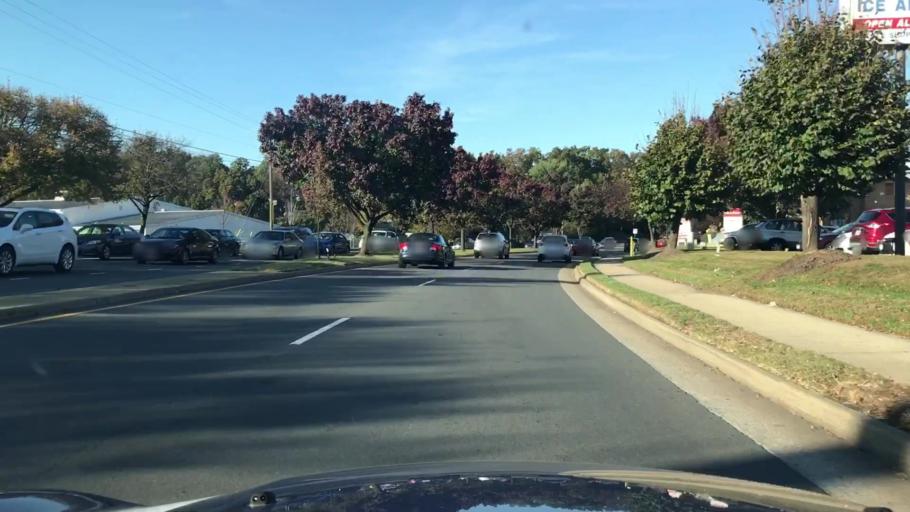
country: US
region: Virginia
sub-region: Fairfax County
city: Mantua
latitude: 38.8486
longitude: -77.2730
